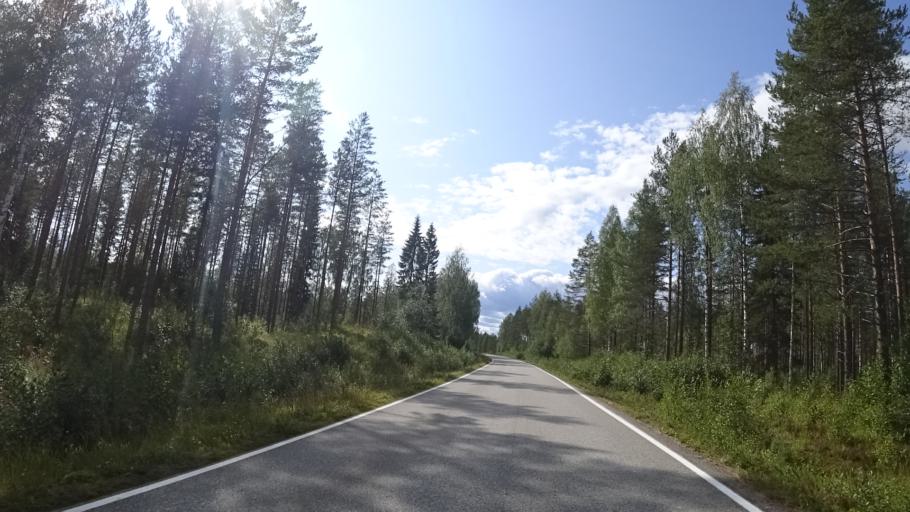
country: FI
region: North Karelia
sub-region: Joensuu
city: Ilomantsi
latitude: 62.4127
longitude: 30.9834
